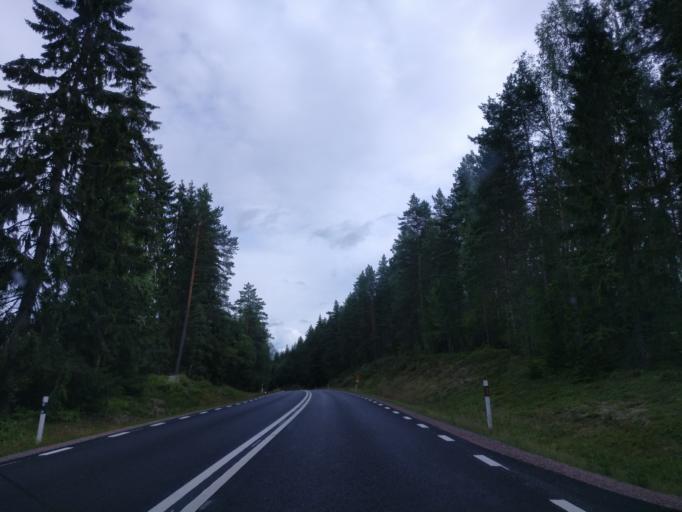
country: SE
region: Vaermland
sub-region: Hagfors Kommun
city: Hagfors
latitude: 60.0573
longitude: 13.5543
